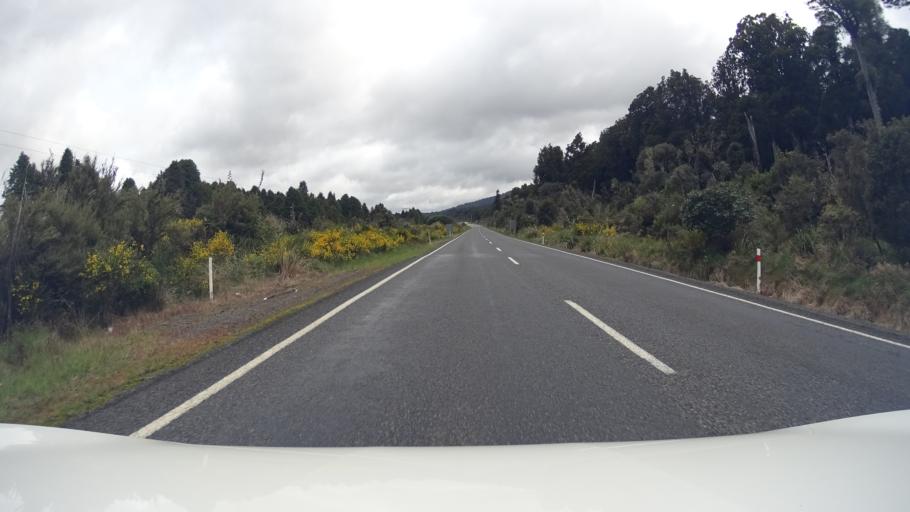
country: NZ
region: Manawatu-Wanganui
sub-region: Ruapehu District
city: Waiouru
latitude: -39.2462
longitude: 175.3894
